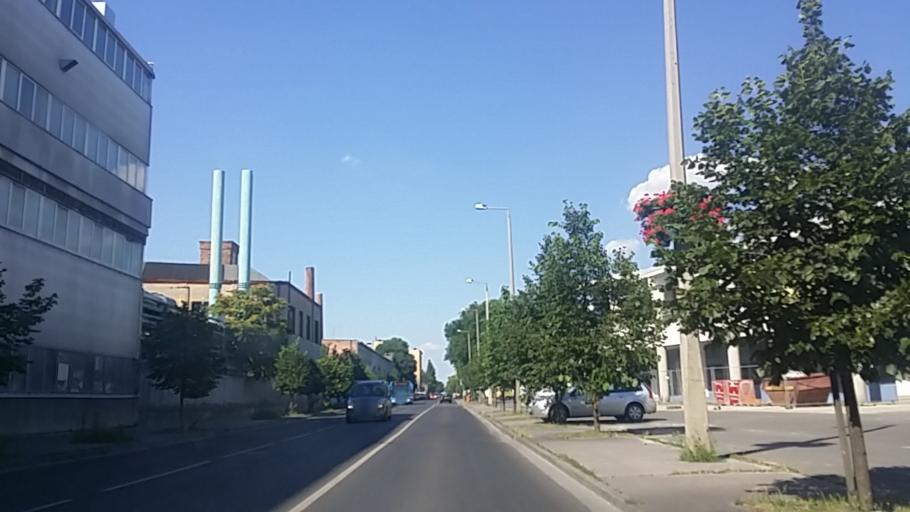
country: HU
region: Budapest
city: Budapest IV. keruelet
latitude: 47.5750
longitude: 19.0829
